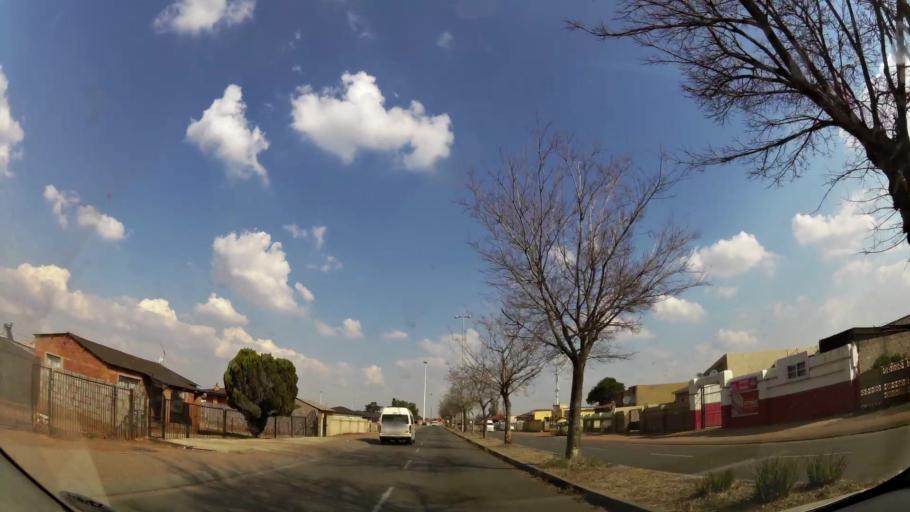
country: ZA
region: Gauteng
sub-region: Ekurhuleni Metropolitan Municipality
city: Germiston
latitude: -26.3211
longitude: 28.1569
